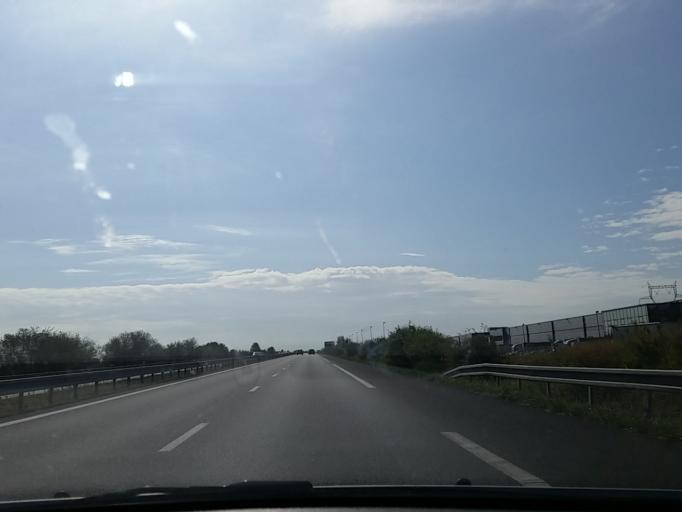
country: FR
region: Centre
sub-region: Departement du Cher
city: La Chapelle-Saint-Ursin
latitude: 47.0523
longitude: 2.3182
